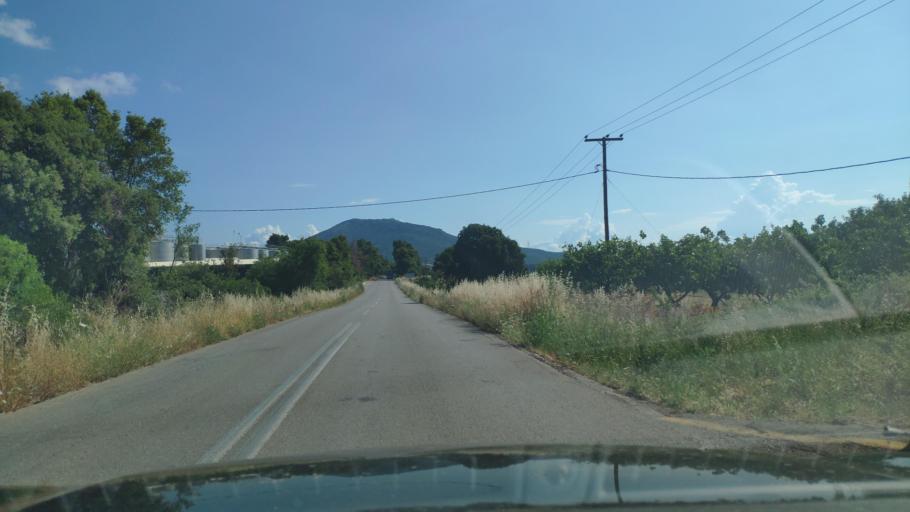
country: GR
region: Central Greece
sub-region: Nomos Voiotias
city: Arma
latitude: 38.3961
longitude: 23.5114
